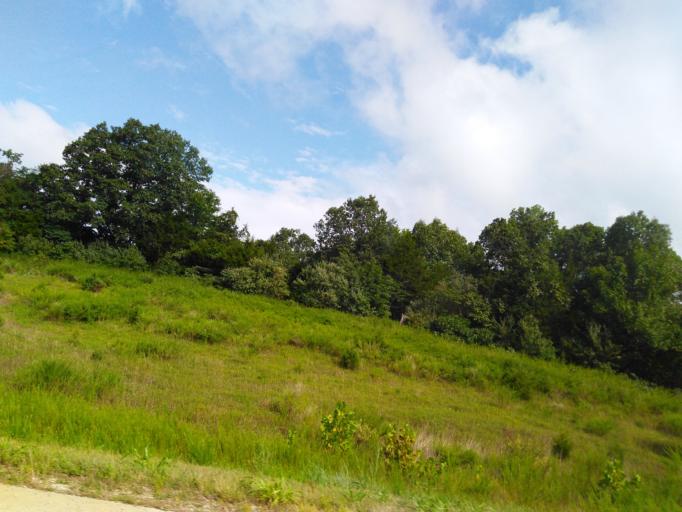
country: US
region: Missouri
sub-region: Jefferson County
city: Hillsboro
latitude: 38.3096
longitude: -90.5388
